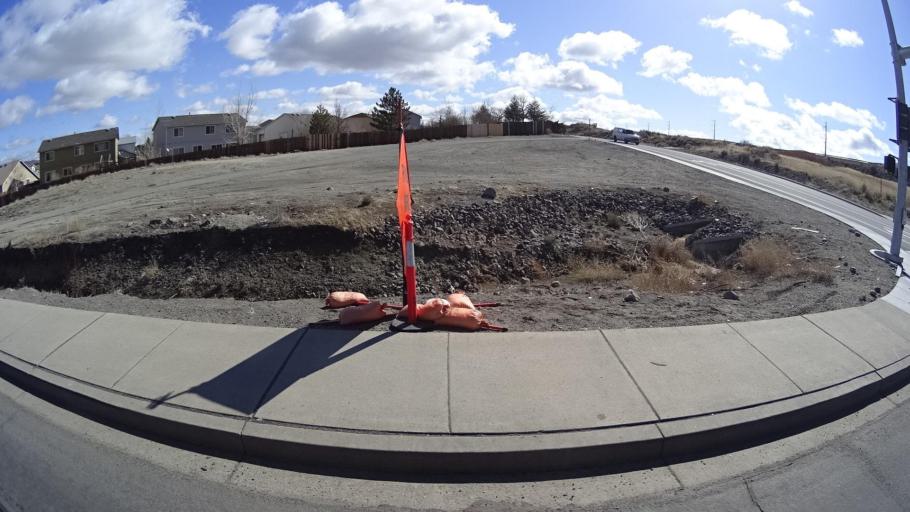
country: US
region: Nevada
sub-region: Washoe County
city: Lemmon Valley
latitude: 39.6280
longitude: -119.9154
